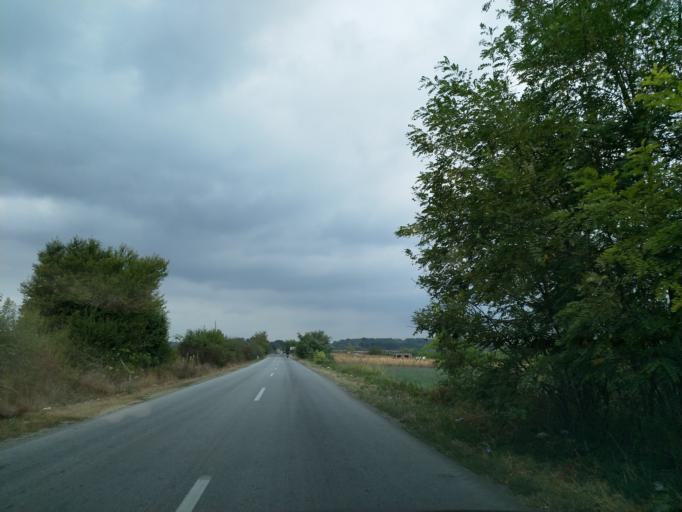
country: RS
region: Central Serbia
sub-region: Pomoravski Okrug
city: Jagodina
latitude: 43.9990
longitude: 21.2163
